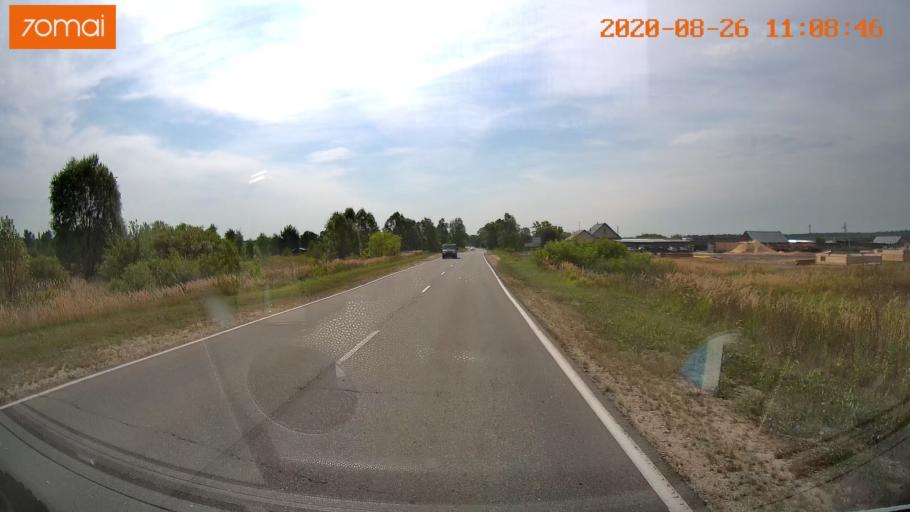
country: RU
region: Rjazan
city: Izhevskoye
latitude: 54.4994
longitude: 41.1227
